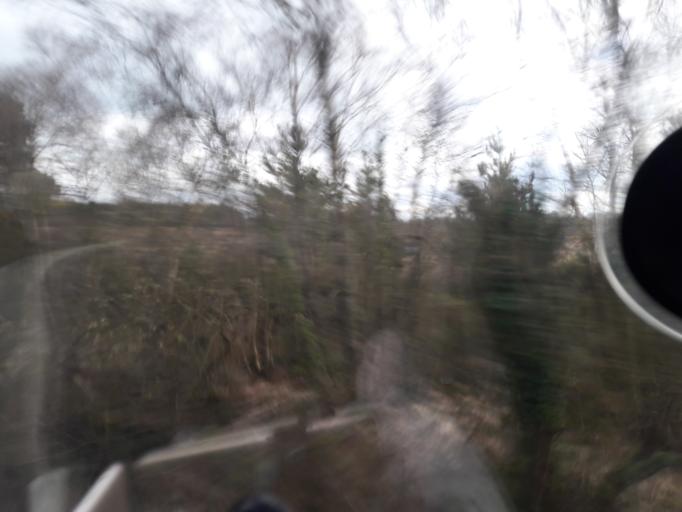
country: IE
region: Leinster
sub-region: An Iarmhi
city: Rochfortbridge
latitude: 53.4998
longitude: -7.2562
